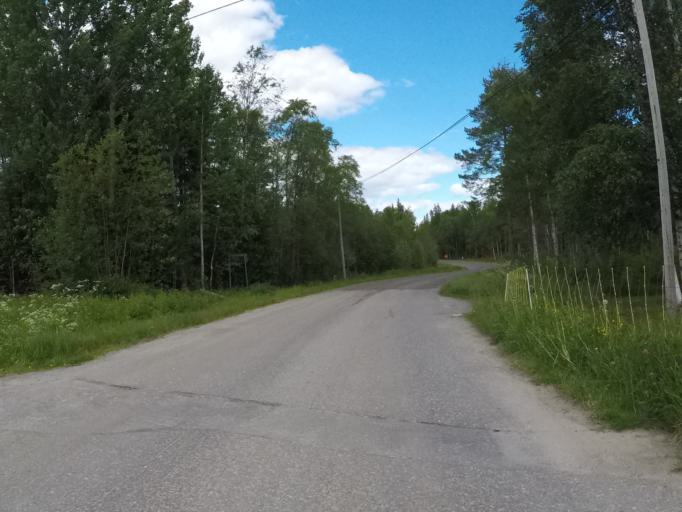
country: SE
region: Vaesterbotten
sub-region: Robertsfors Kommun
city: Robertsfors
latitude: 63.9952
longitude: 20.8894
